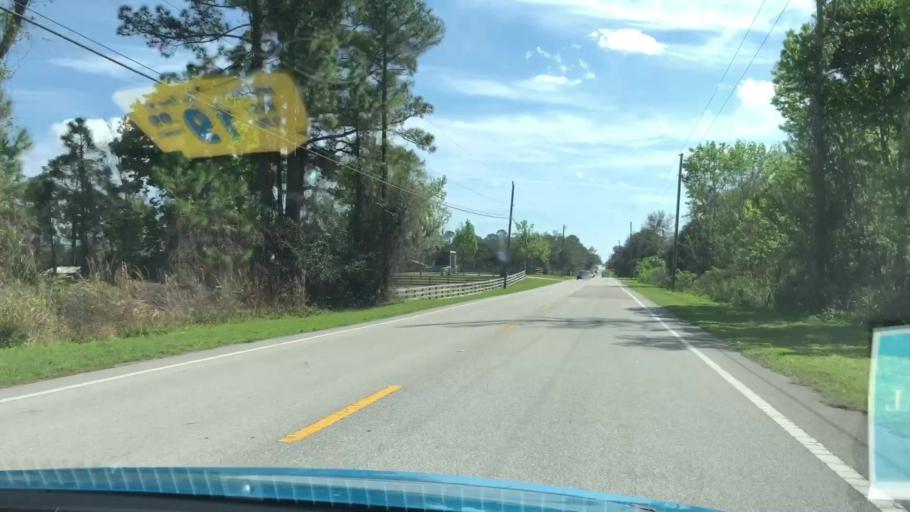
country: US
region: Florida
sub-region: Volusia County
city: Deltona
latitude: 28.8620
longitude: -81.2053
